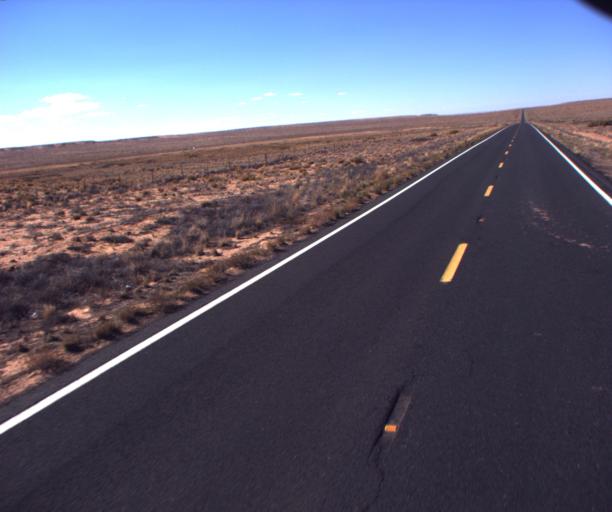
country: US
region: Arizona
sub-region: Coconino County
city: Tuba City
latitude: 36.0269
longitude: -111.1515
